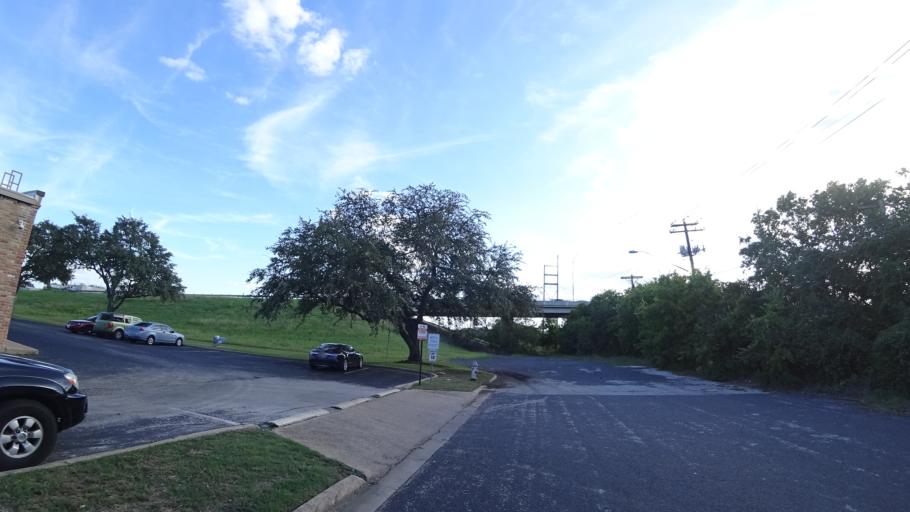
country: US
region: Texas
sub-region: Williamson County
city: Jollyville
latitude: 30.3619
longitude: -97.7428
